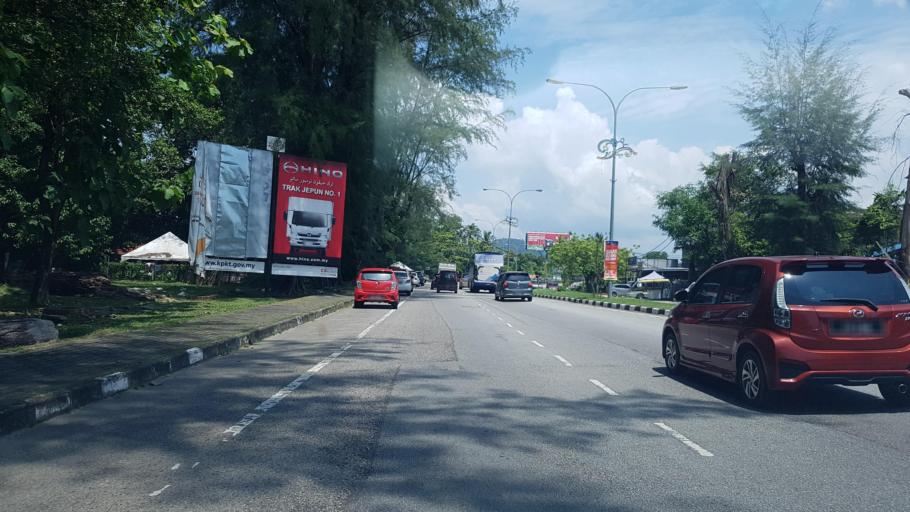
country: MY
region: Terengganu
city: Kuala Terengganu
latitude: 5.2830
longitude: 103.1691
